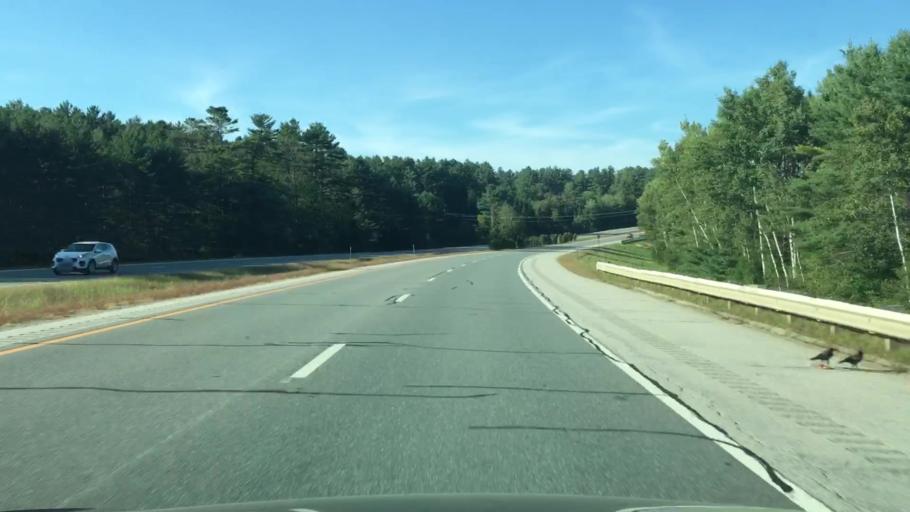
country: US
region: New Hampshire
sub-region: Grafton County
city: Littleton
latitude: 44.2482
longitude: -71.7611
